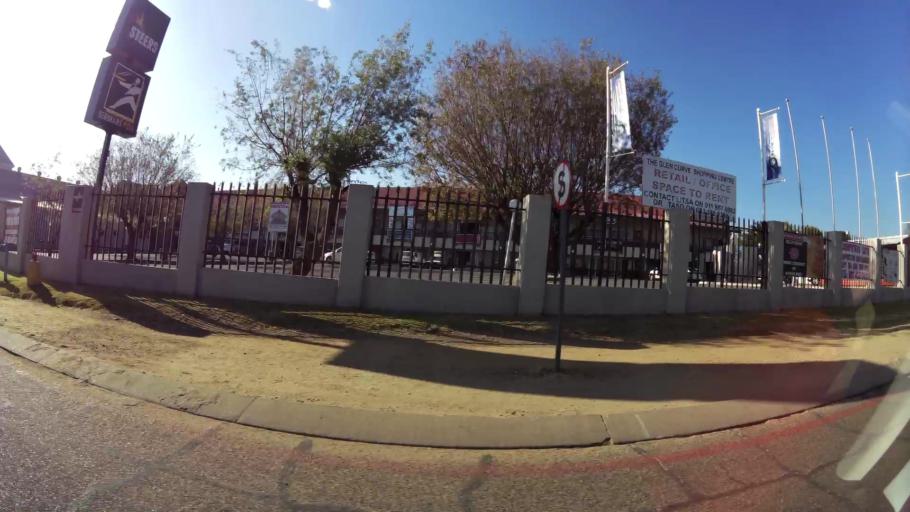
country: ZA
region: Gauteng
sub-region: City of Johannesburg Metropolitan Municipality
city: Modderfontein
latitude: -26.1386
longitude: 28.1375
